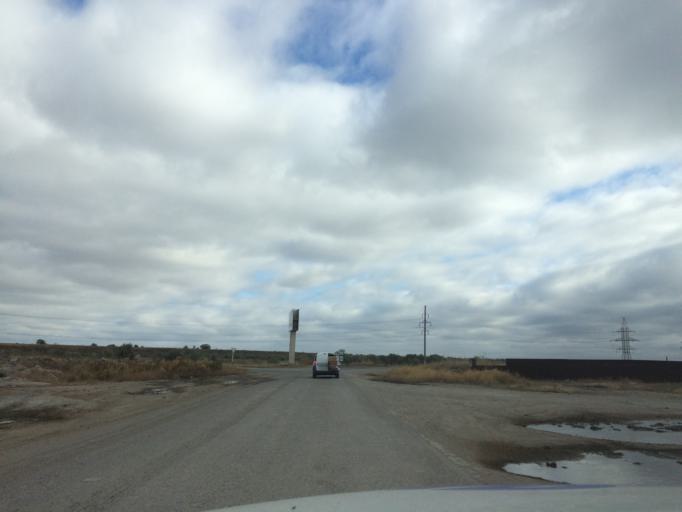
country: KZ
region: Astana Qalasy
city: Astana
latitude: 51.2095
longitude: 71.4448
